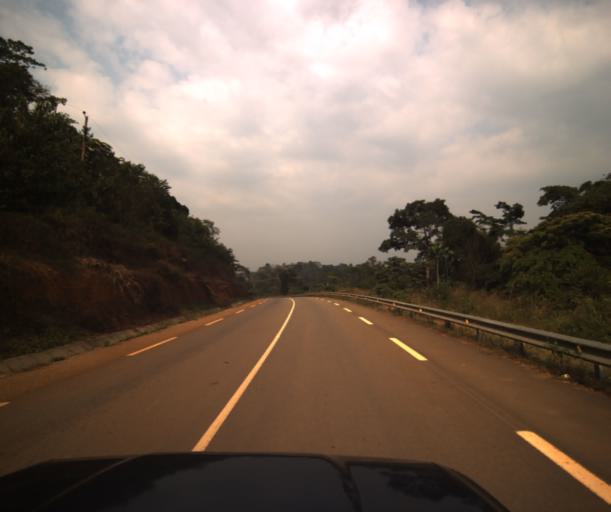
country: CM
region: Centre
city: Mbankomo
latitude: 3.7691
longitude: 11.4126
